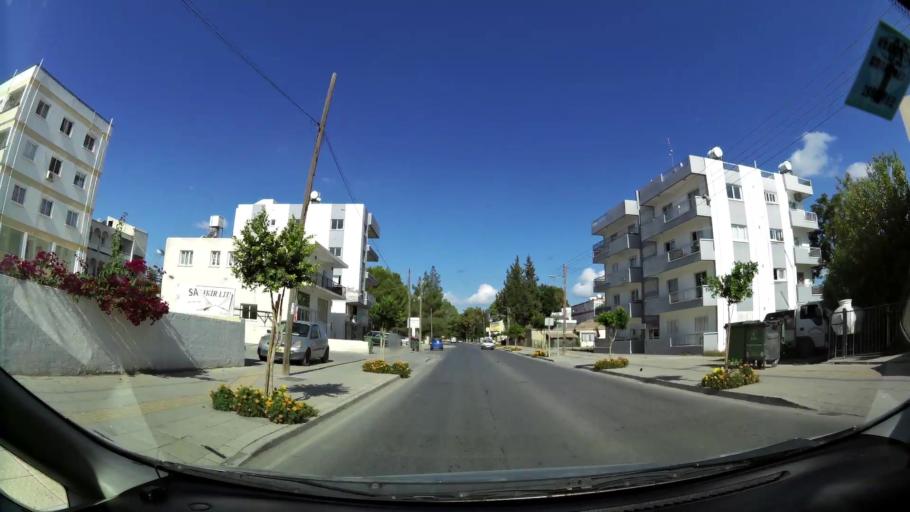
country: CY
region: Lefkosia
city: Nicosia
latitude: 35.2127
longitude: 33.3103
